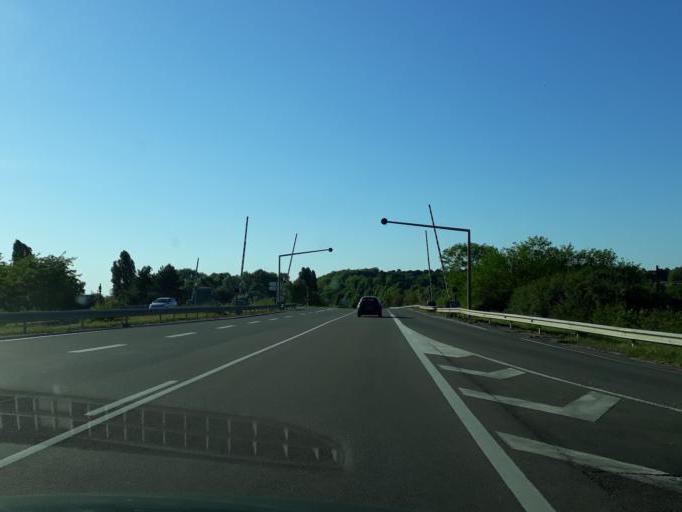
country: FR
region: Bourgogne
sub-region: Departement de la Nievre
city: Neuvy-sur-Loire
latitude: 47.5194
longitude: 2.8803
